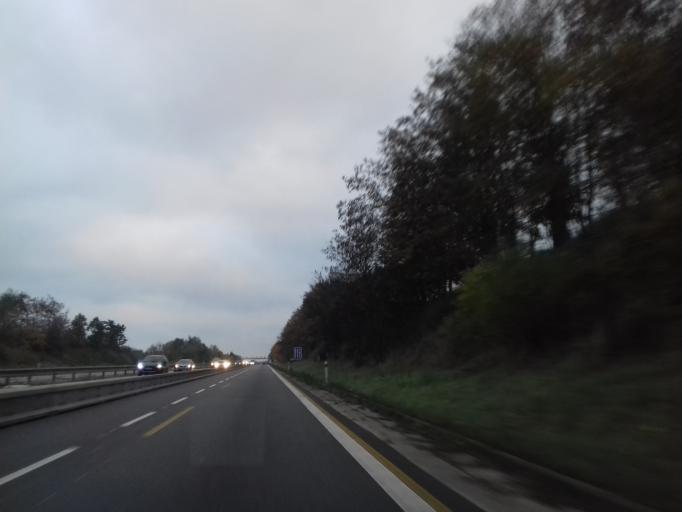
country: CZ
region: Central Bohemia
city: Trhovy Stepanov
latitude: 49.7340
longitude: 15.0424
